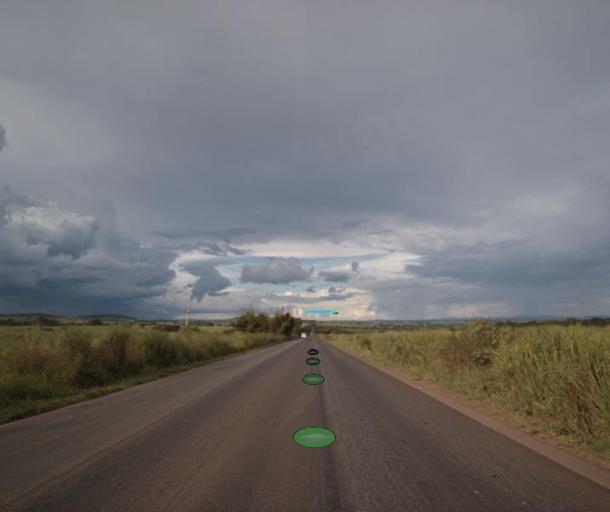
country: BR
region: Goias
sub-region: Ceres
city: Ceres
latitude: -15.1420
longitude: -49.5277
